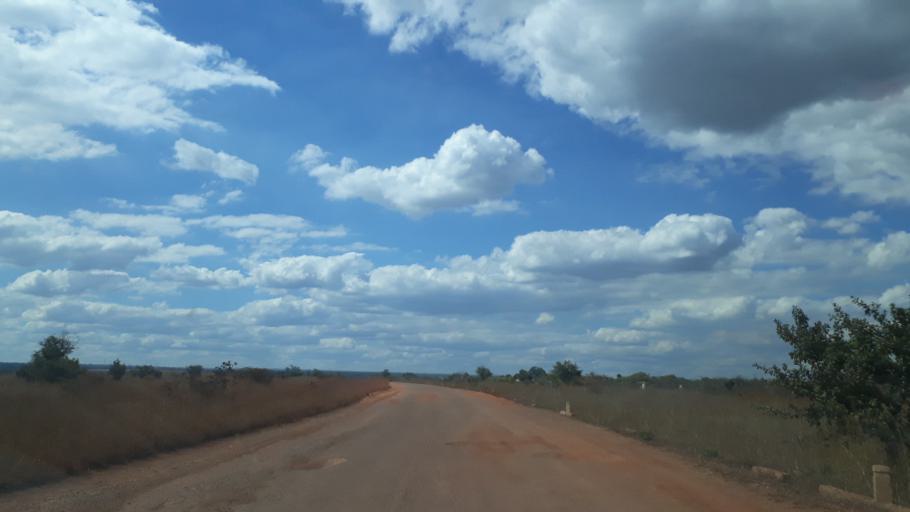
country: ZM
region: Copperbelt
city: Mufulira
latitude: -11.9935
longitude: 28.7282
